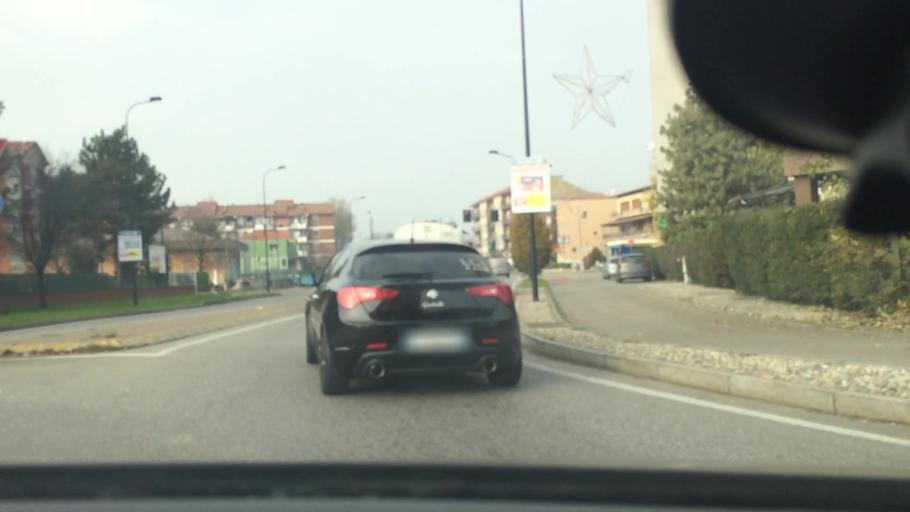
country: IT
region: Lombardy
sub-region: Provincia di Monza e Brianza
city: Villaggio del Sole
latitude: 45.6173
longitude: 9.1199
